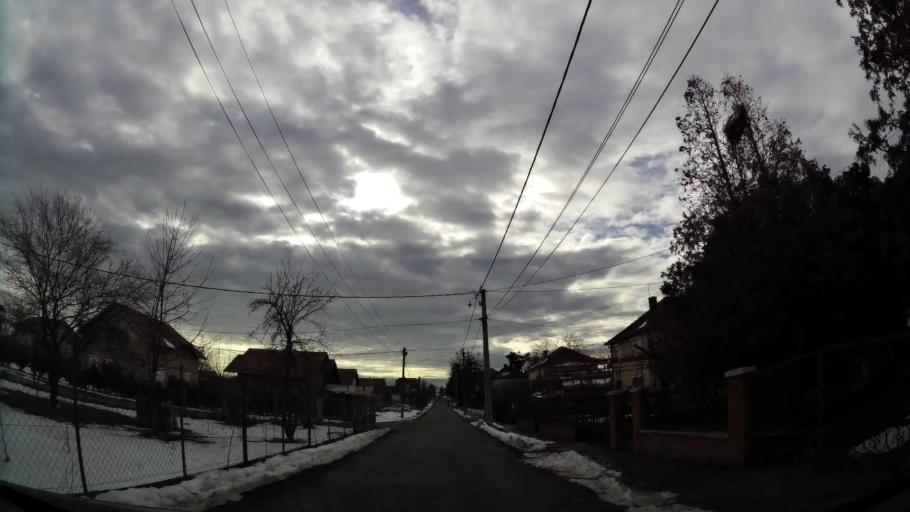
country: RS
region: Central Serbia
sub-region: Belgrade
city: Surcin
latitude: 44.7996
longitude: 20.2968
